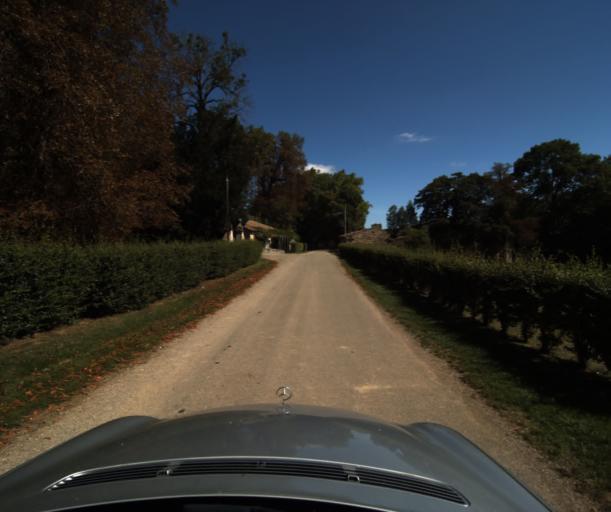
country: FR
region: Midi-Pyrenees
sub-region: Departement de l'Ariege
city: Lavelanet
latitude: 42.9895
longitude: 1.9120
